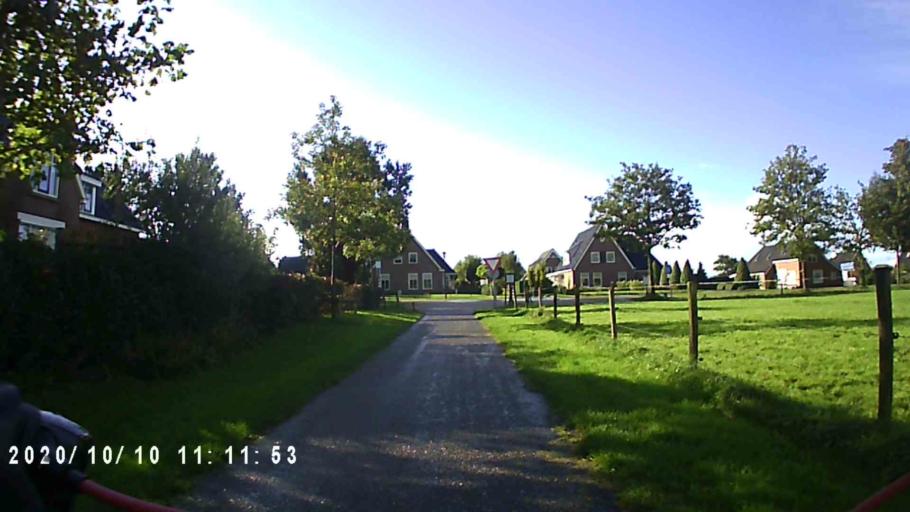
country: NL
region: Friesland
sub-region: Gemeente Smallingerland
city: Drachtstercompagnie
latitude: 53.1121
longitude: 6.2050
